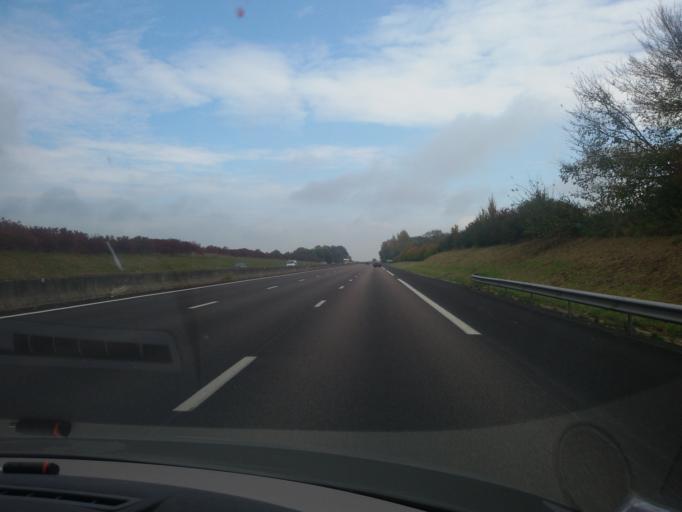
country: FR
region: Haute-Normandie
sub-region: Departement de l'Eure
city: Hauville
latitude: 49.3680
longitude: 0.7828
